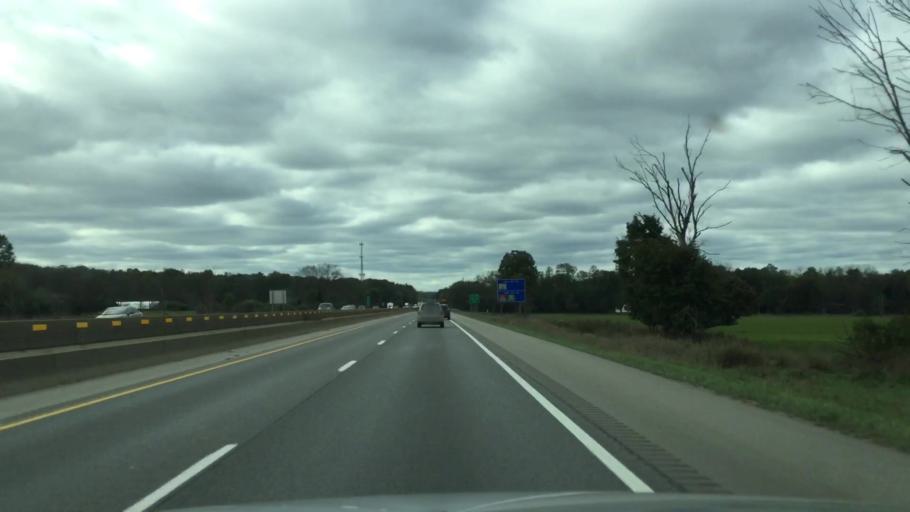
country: US
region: Michigan
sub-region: Kalamazoo County
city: Galesburg
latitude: 42.2786
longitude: -85.4027
